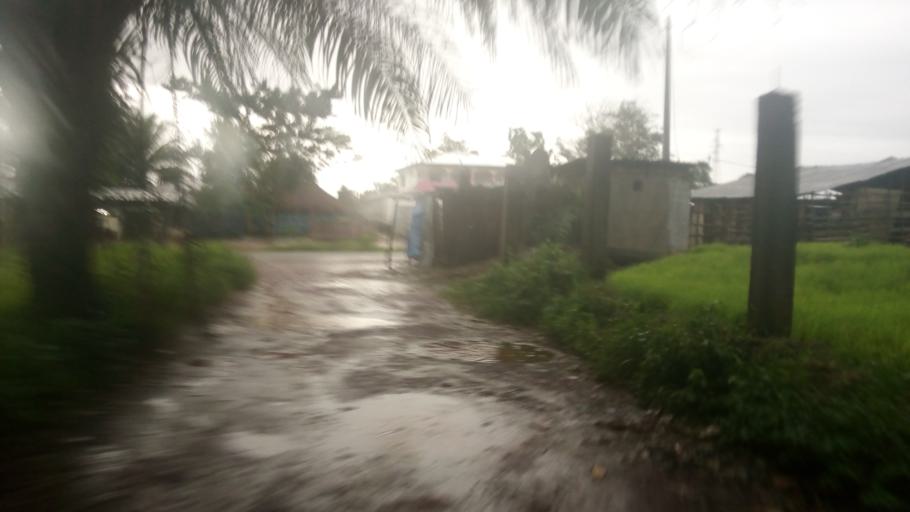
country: SL
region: Northern Province
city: Lunsar
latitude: 8.6925
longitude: -12.5337
